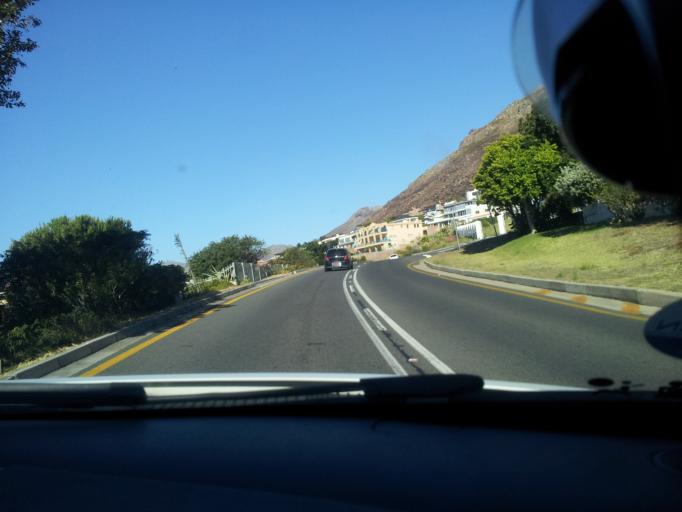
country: ZA
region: Western Cape
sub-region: Overberg District Municipality
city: Grabouw
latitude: -34.1628
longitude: 18.8673
